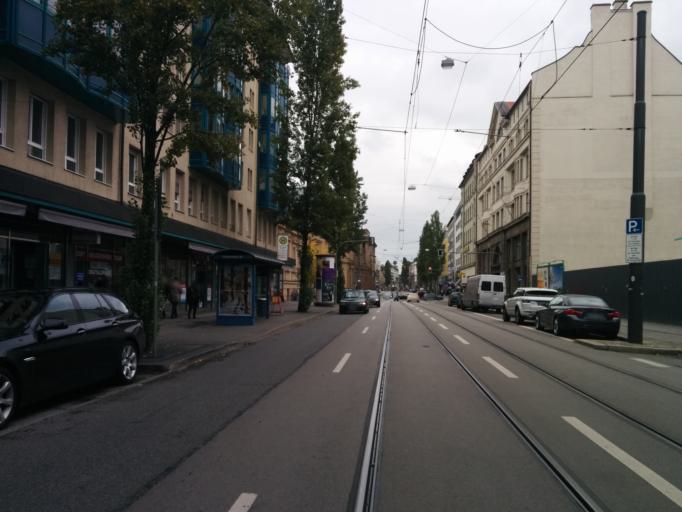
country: DE
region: Bavaria
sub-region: Upper Bavaria
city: Munich
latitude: 48.1392
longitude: 11.5544
